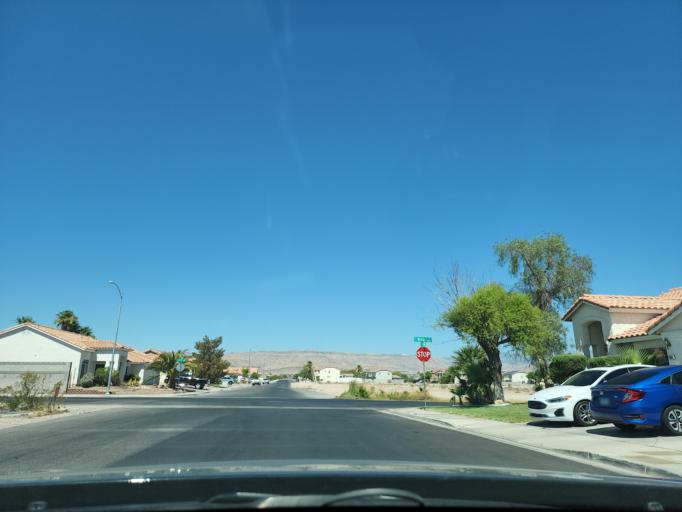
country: US
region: Nevada
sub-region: Clark County
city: Spring Valley
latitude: 36.0810
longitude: -115.2633
